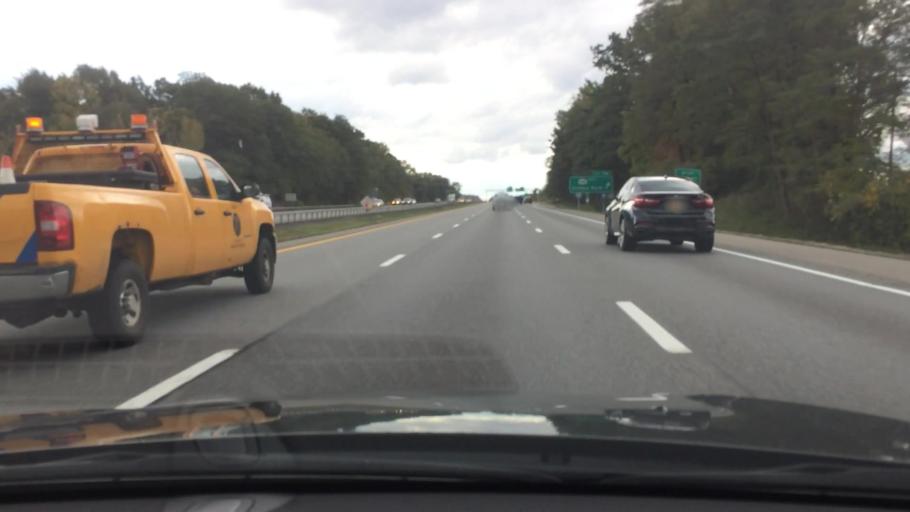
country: US
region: New York
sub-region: Saratoga County
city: Country Knolls
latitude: 42.8688
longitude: -73.7765
